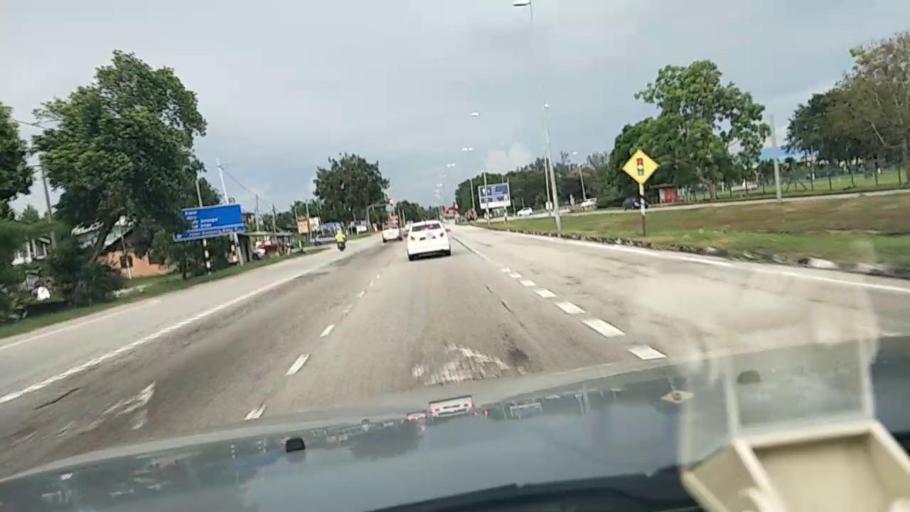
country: MY
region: Perak
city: Kampong Dungun
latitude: 3.1264
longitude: 101.3712
